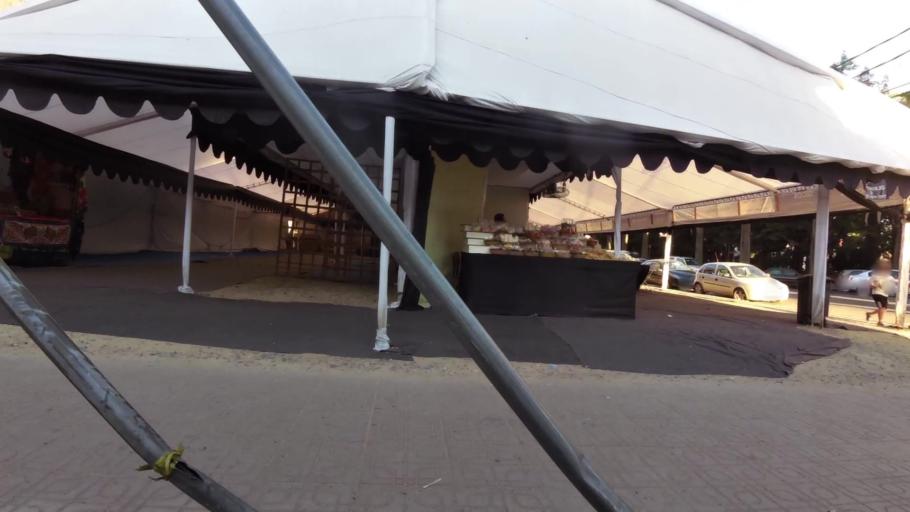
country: CL
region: Maule
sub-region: Provincia de Curico
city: Curico
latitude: -34.9847
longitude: -71.2401
